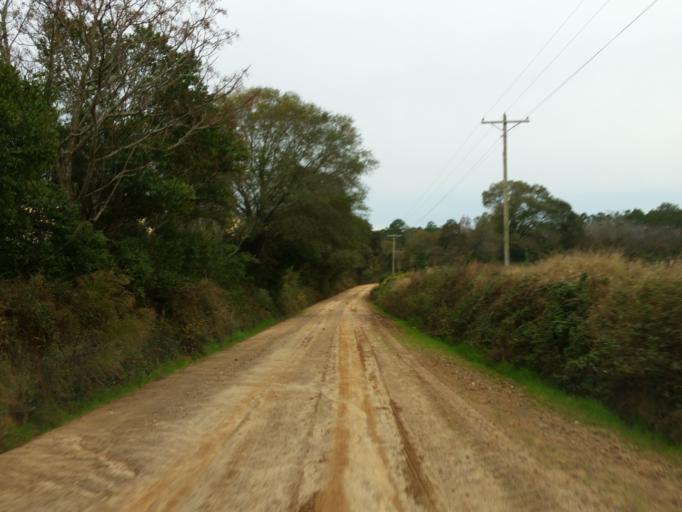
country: US
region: Georgia
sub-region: Crisp County
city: Cordele
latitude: 31.8674
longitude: -83.7297
